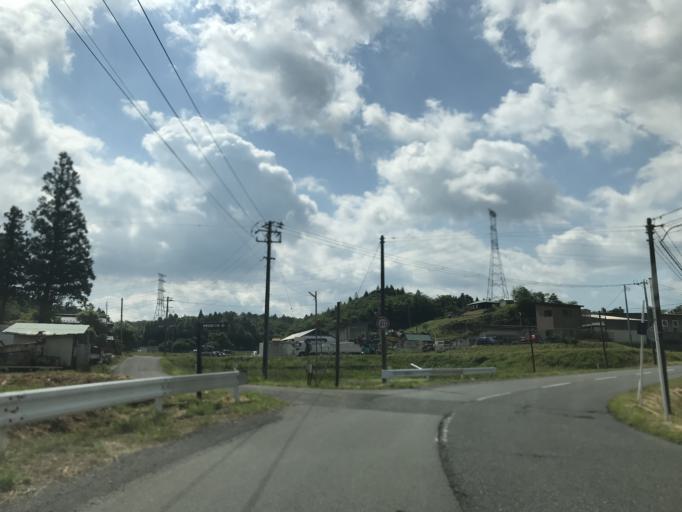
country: JP
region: Miyagi
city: Furukawa
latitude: 38.7816
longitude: 140.9590
